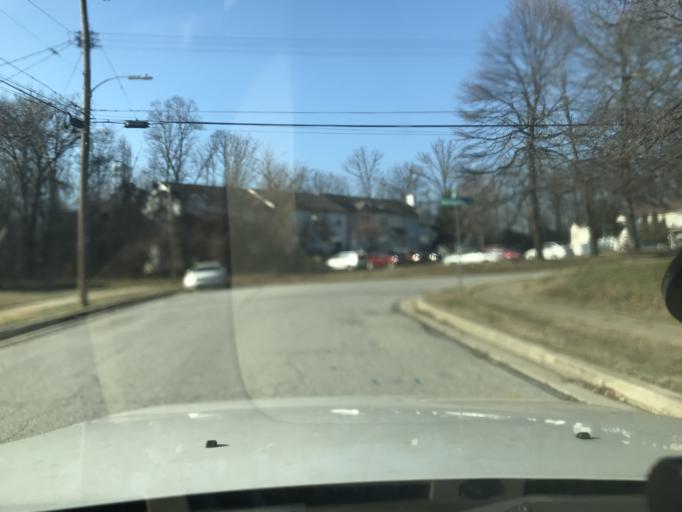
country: US
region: Maryland
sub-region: Baltimore County
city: Owings Mills
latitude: 39.4185
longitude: -76.7958
